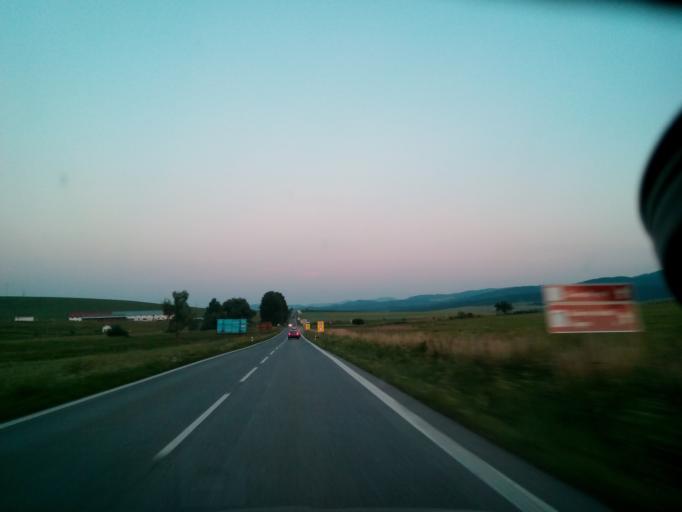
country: SK
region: Kosicky
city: Spisska Nova Ves
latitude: 48.9771
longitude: 20.4877
